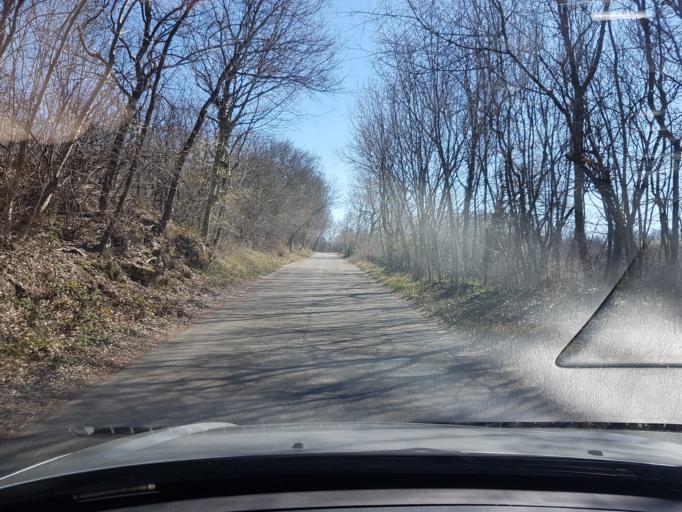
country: IT
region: Friuli Venezia Giulia
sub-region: Provincia di Trieste
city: Sistiana-Visogliano
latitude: 45.7882
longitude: 13.6479
